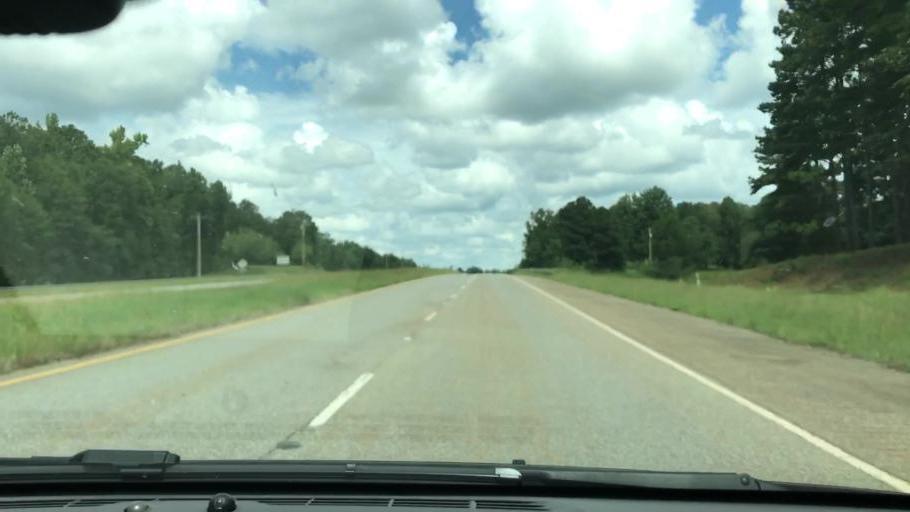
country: US
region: Georgia
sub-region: Stewart County
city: Lumpkin
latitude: 32.1294
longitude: -84.8246
